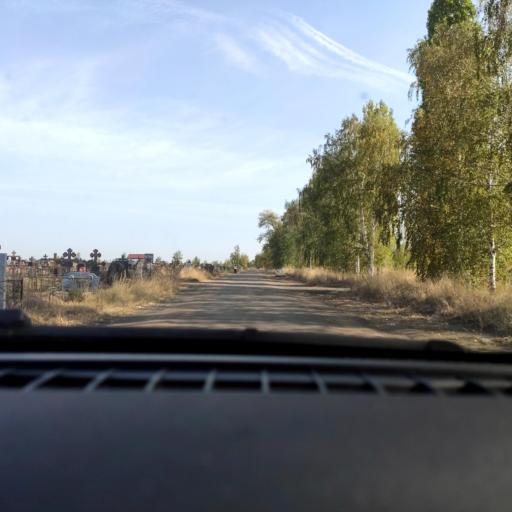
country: RU
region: Voronezj
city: Maslovka
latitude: 51.5129
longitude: 39.1987
